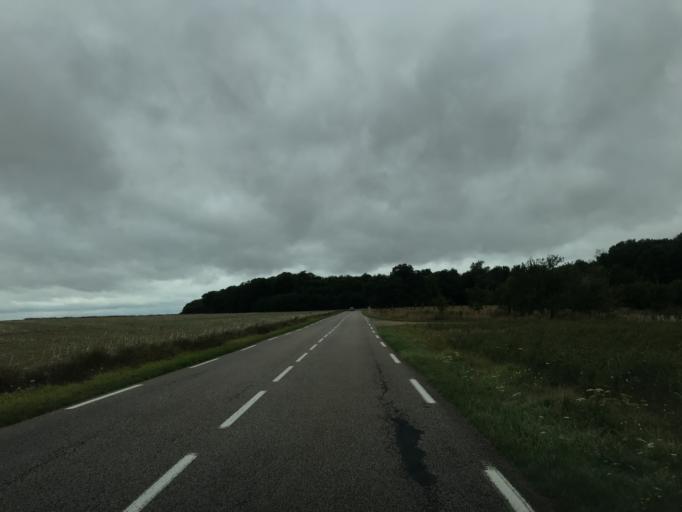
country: FR
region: Haute-Normandie
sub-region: Departement de l'Eure
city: Menilles
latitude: 49.0323
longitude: 1.2743
